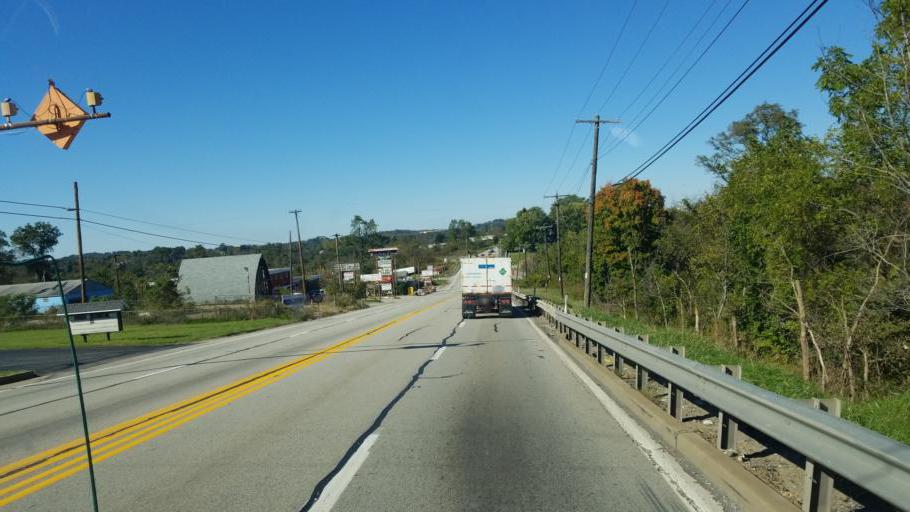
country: US
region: Pennsylvania
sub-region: Westmoreland County
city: Trafford
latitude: 40.3470
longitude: -79.7655
